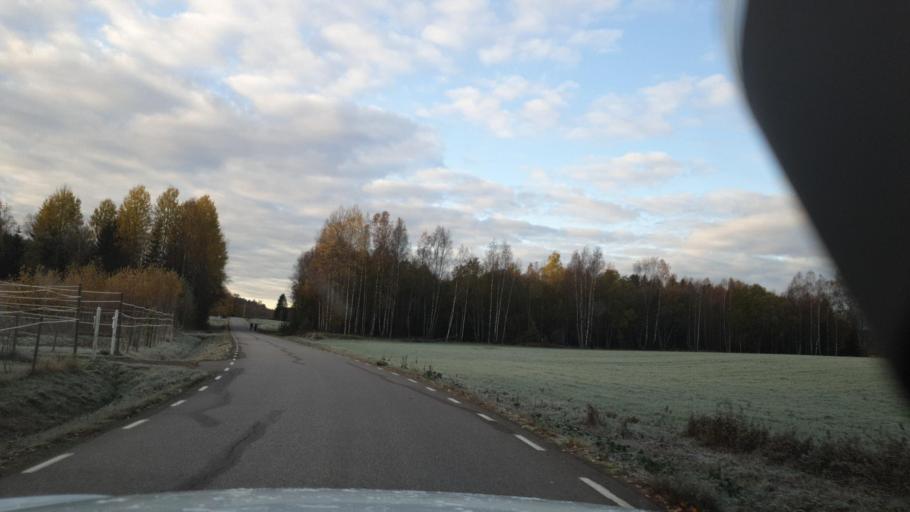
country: SE
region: Vaermland
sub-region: Eda Kommun
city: Amotfors
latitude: 59.7239
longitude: 12.1628
